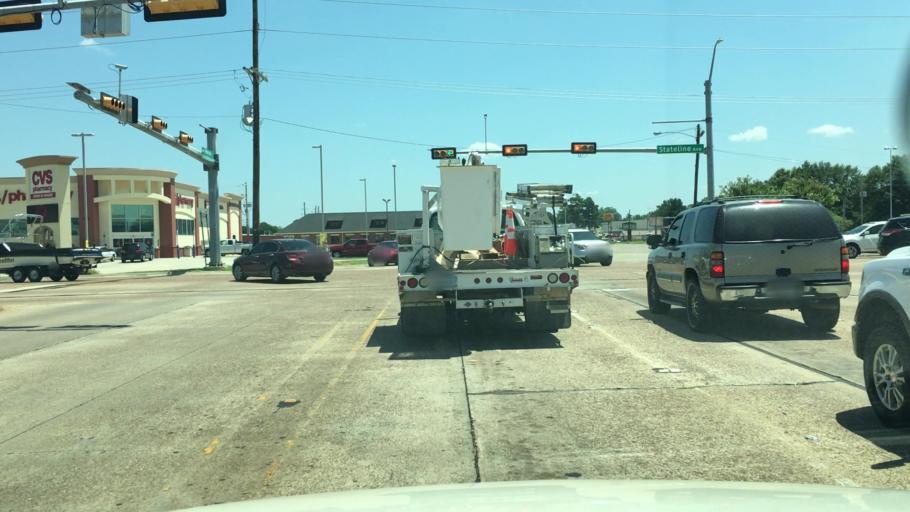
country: US
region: Arkansas
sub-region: Miller County
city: Texarkana
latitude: 33.4606
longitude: -94.0435
